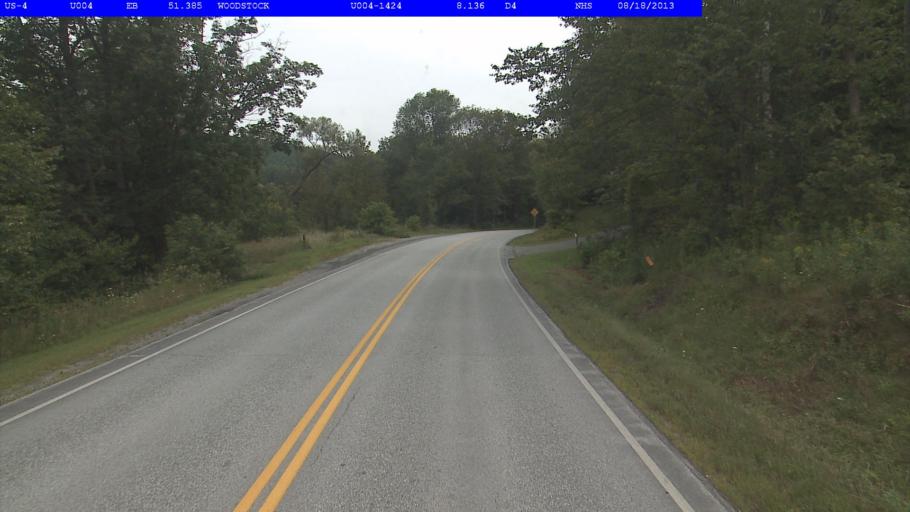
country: US
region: Vermont
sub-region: Windsor County
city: Woodstock
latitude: 43.6381
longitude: -72.4905
